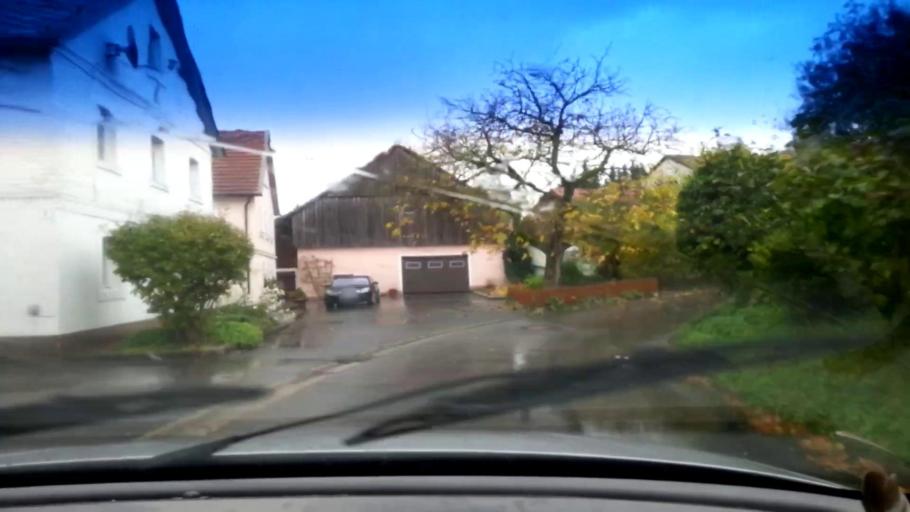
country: DE
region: Bavaria
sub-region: Upper Franconia
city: Stadelhofen
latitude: 50.0033
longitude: 11.1982
